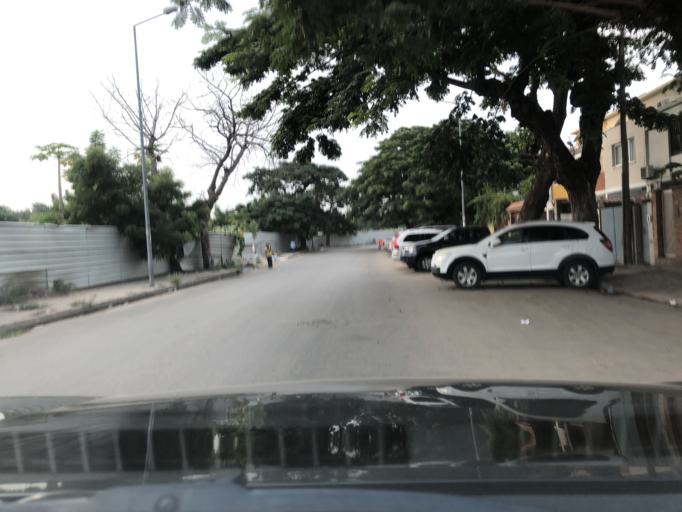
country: AO
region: Luanda
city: Luanda
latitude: -8.8310
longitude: 13.2545
